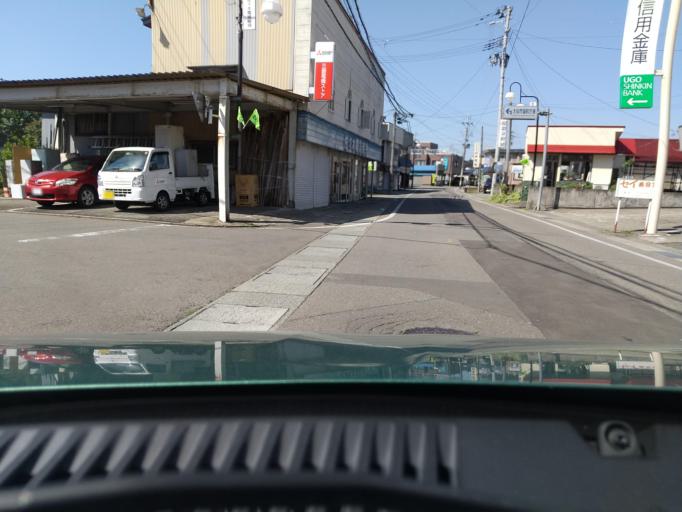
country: JP
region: Akita
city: Akita
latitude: 39.6167
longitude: 140.3220
